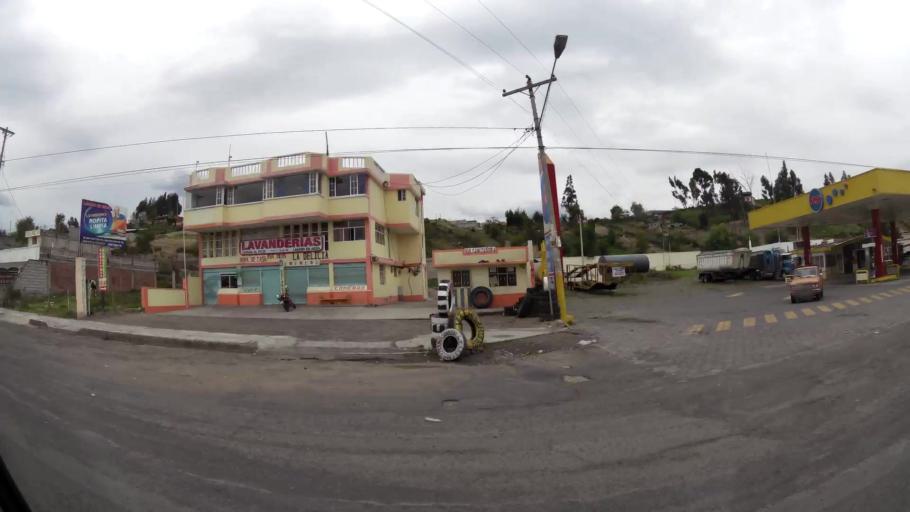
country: EC
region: Cotopaxi
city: Latacunga
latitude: -0.9648
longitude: -78.6109
